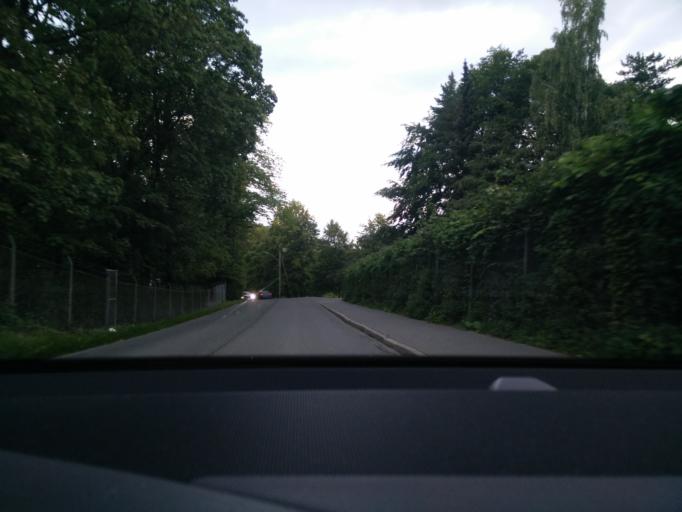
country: NO
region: Oslo
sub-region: Oslo
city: Sjolyststranda
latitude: 59.9098
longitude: 10.6805
